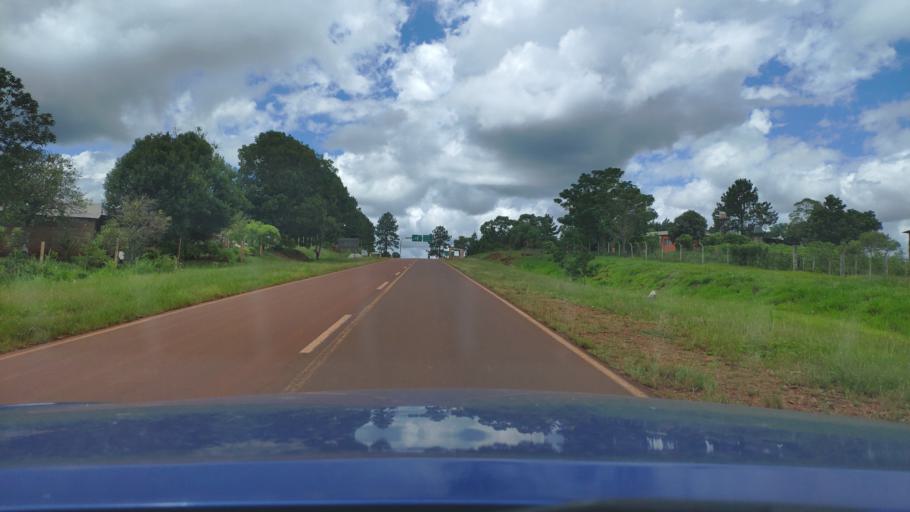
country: AR
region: Misiones
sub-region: Departamento de San Javier
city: San Javier
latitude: -27.8395
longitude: -55.2243
